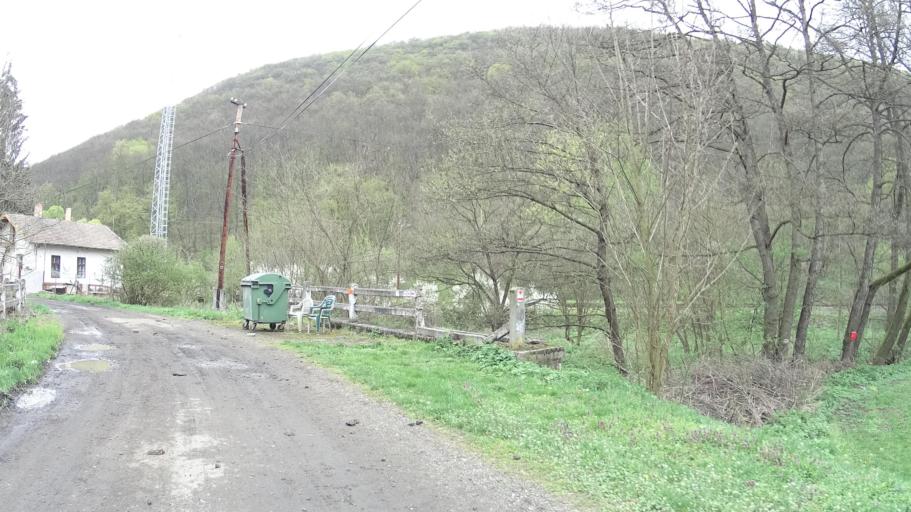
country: HU
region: Pest
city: Kismaros
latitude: 47.8705
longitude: 19.0303
